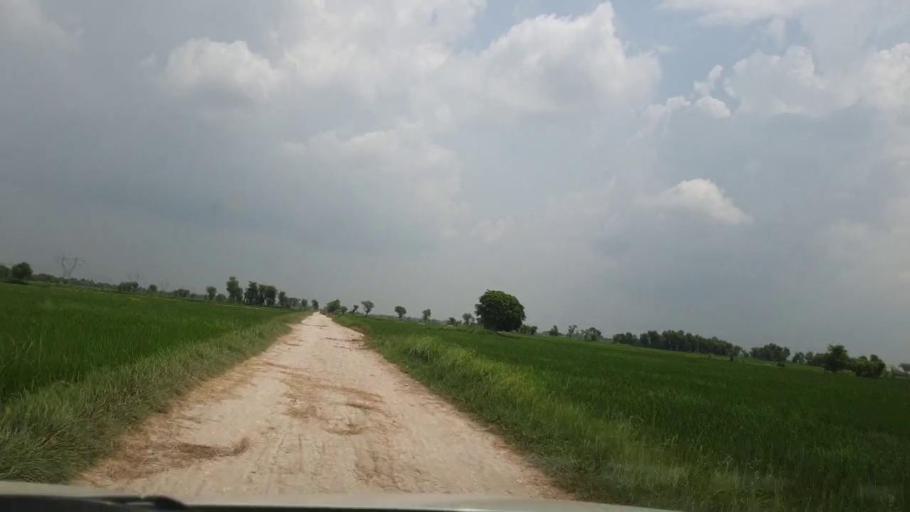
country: PK
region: Sindh
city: Goth Garelo
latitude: 27.4129
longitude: 68.0709
